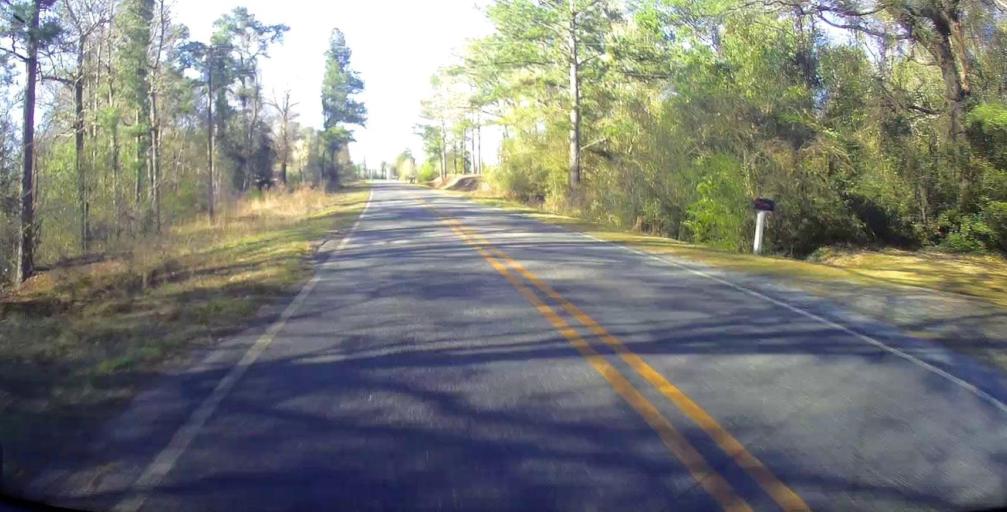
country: US
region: Georgia
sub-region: Peach County
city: Fort Valley
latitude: 32.5889
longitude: -83.8514
